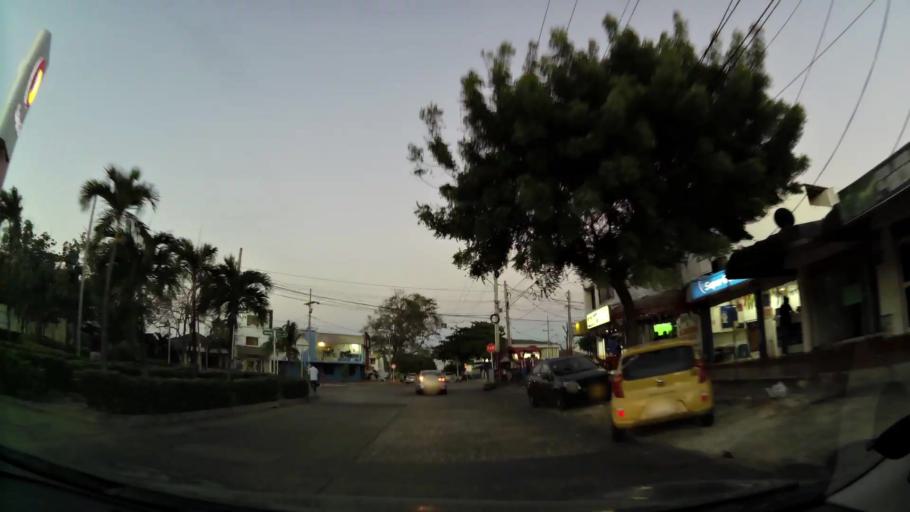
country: CO
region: Atlantico
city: Barranquilla
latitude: 10.9842
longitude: -74.8078
